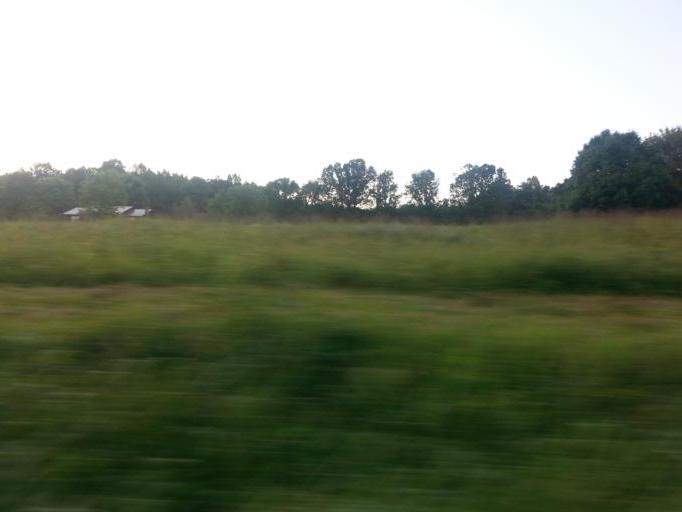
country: US
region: Tennessee
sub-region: Union County
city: Luttrell
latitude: 36.2360
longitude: -83.6978
